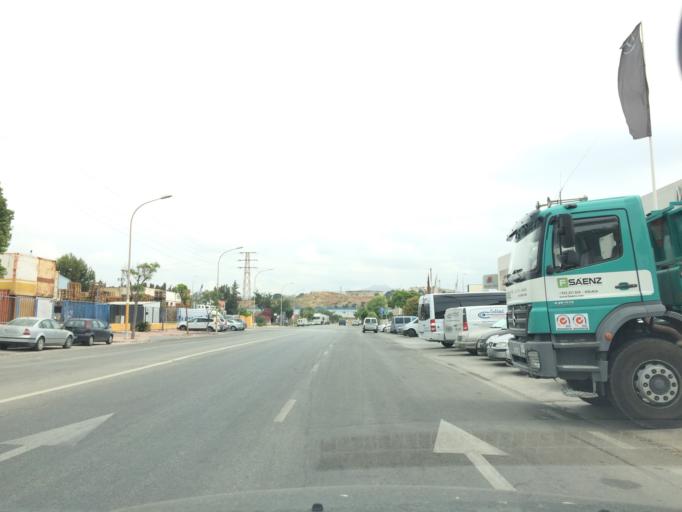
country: ES
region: Andalusia
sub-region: Provincia de Malaga
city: Malaga
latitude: 36.6954
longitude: -4.4840
